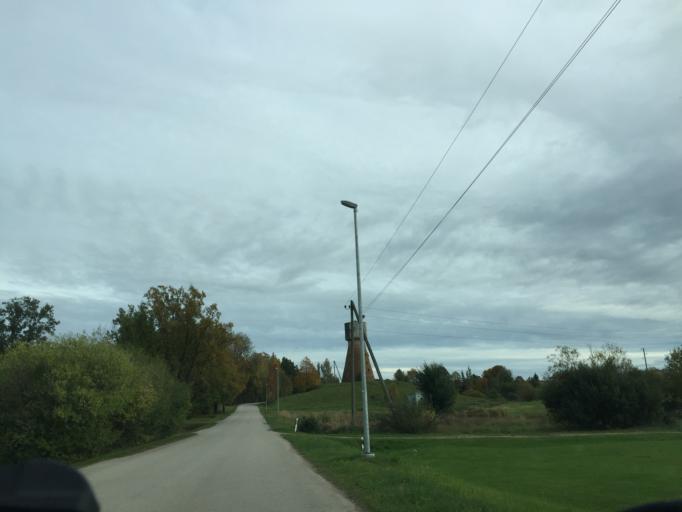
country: LV
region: Auces Novads
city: Auce
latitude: 56.5435
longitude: 22.9919
